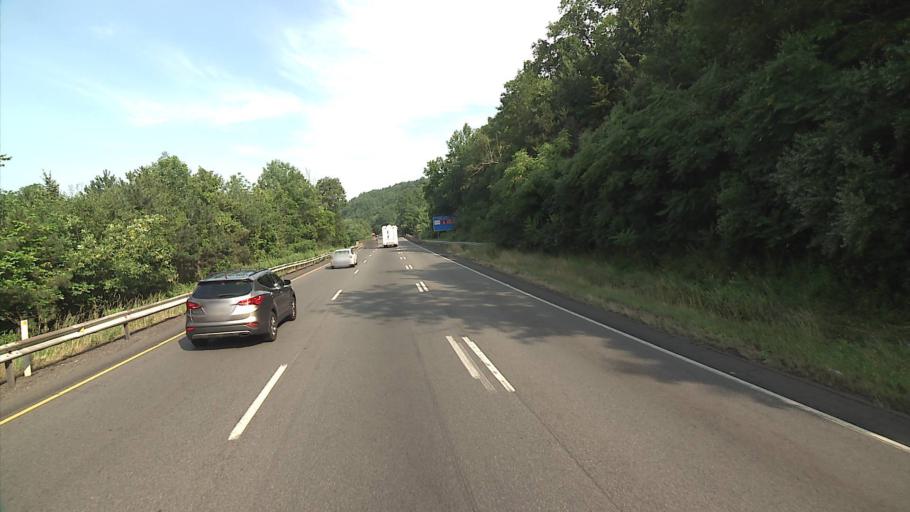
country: US
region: Connecticut
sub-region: New Haven County
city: Meriden
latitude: 41.5493
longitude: -72.8280
